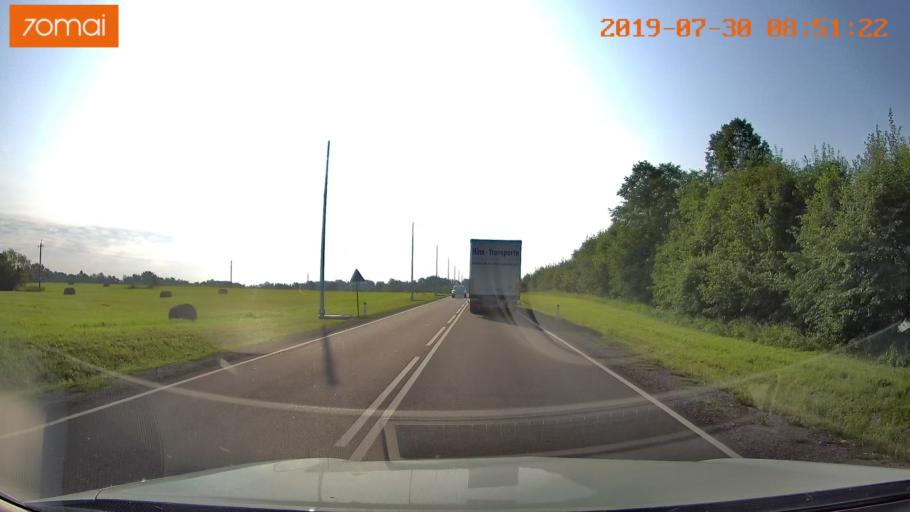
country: RU
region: Kaliningrad
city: Chernyakhovsk
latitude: 54.6029
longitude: 21.9565
